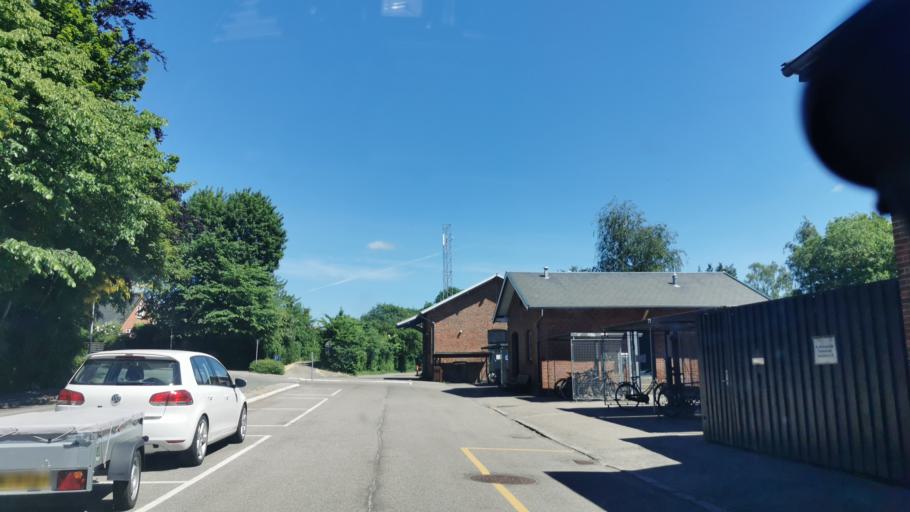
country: DK
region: Capital Region
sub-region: Fredensborg Kommune
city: Fredensborg
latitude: 55.9773
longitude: 12.4070
